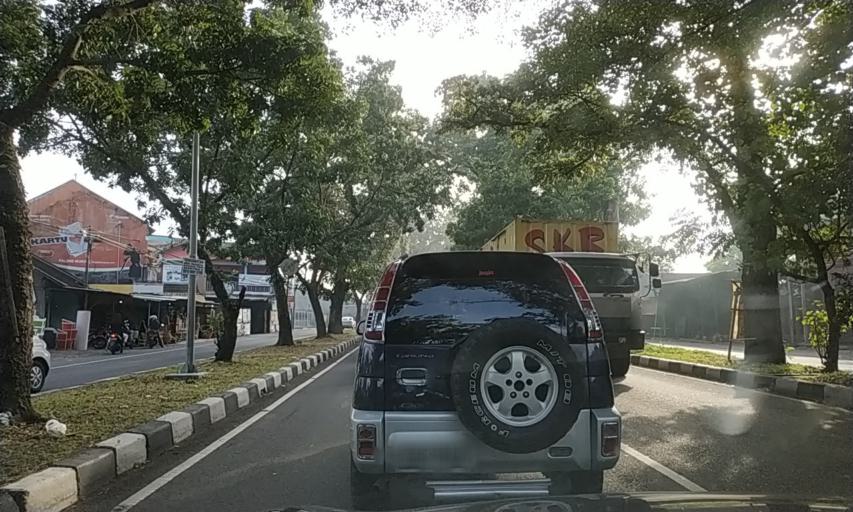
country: ID
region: Central Java
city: Candi Prambanan
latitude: -7.7584
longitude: 110.4791
